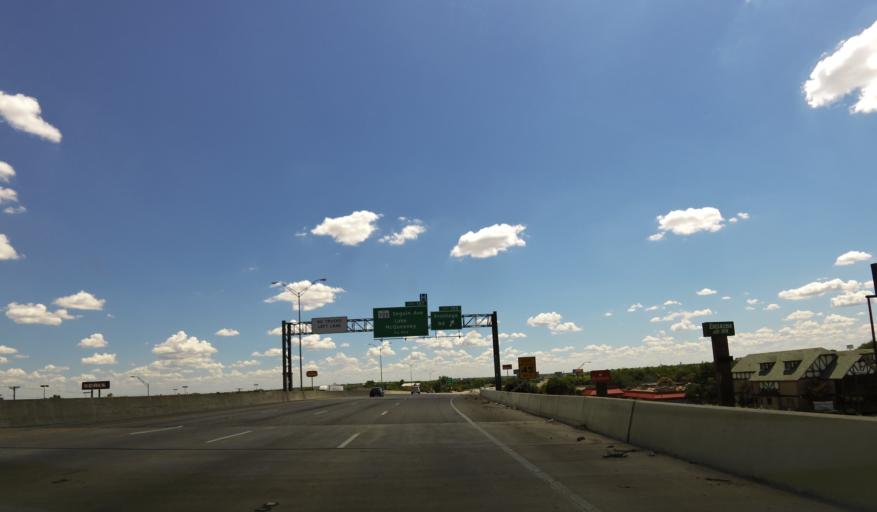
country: US
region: Texas
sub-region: Comal County
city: New Braunfels
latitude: 29.7003
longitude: -98.0941
